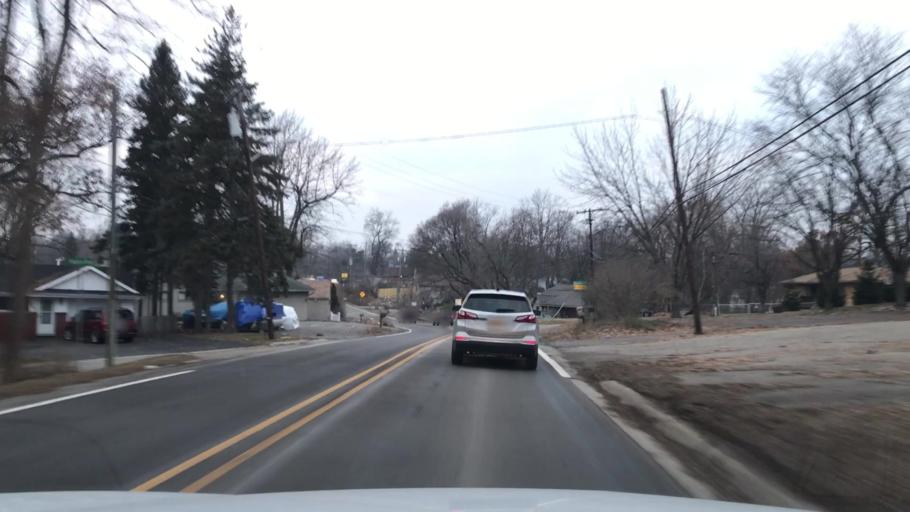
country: US
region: Michigan
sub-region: Oakland County
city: Waterford
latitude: 42.7061
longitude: -83.3743
